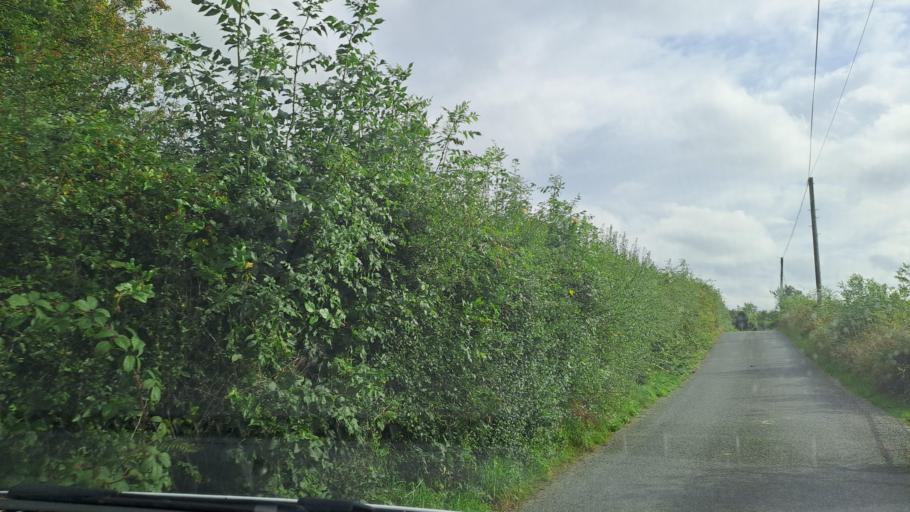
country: IE
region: Ulster
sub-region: An Cabhan
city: Kingscourt
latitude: 53.9857
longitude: -6.8621
